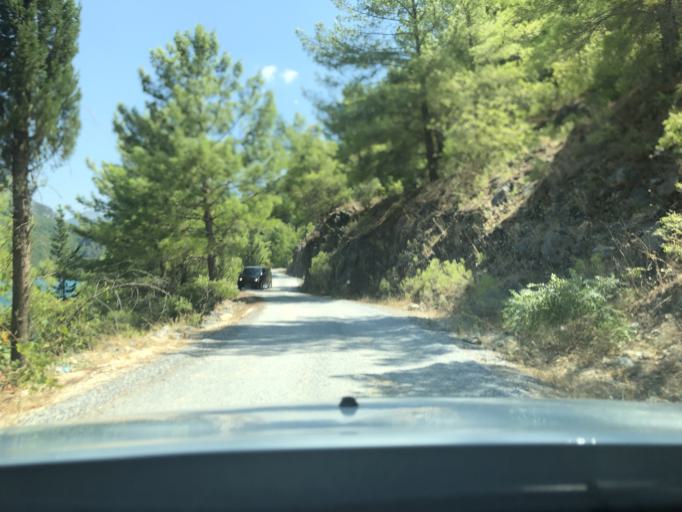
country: TR
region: Antalya
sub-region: Manavgat
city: Manavgat
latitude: 36.9077
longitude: 31.5546
